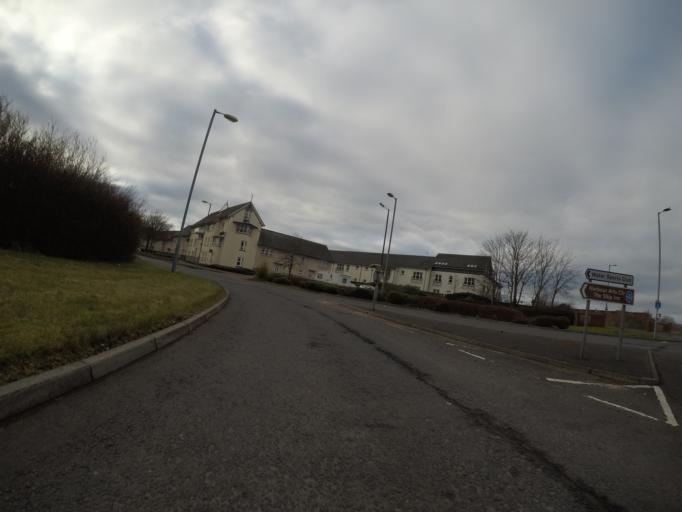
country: GB
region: Scotland
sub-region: North Ayrshire
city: Irvine
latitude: 55.6128
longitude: -4.6763
